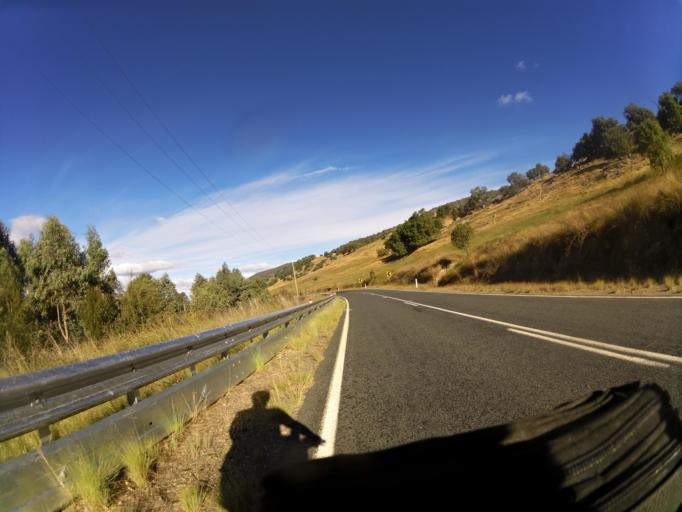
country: AU
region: New South Wales
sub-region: Greater Hume Shire
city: Holbrook
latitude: -35.9659
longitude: 147.7669
